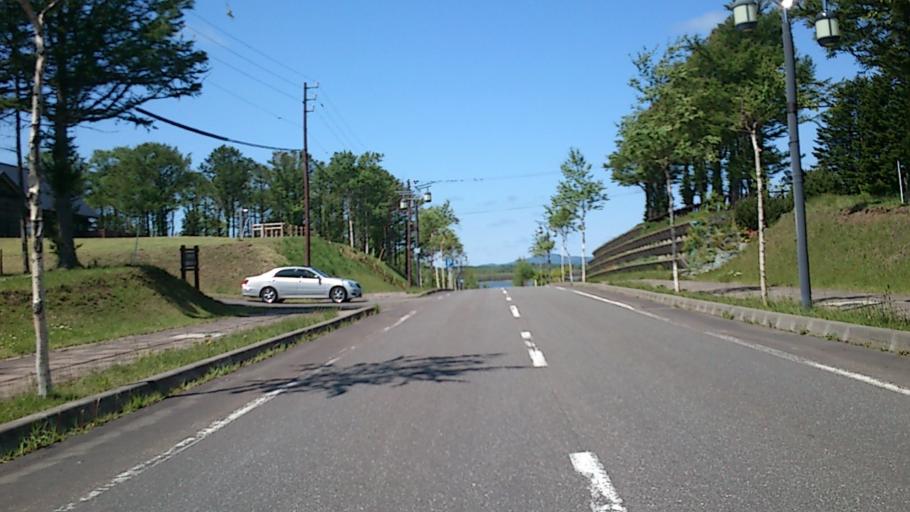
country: JP
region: Hokkaido
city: Makubetsu
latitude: 45.1248
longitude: 142.3502
